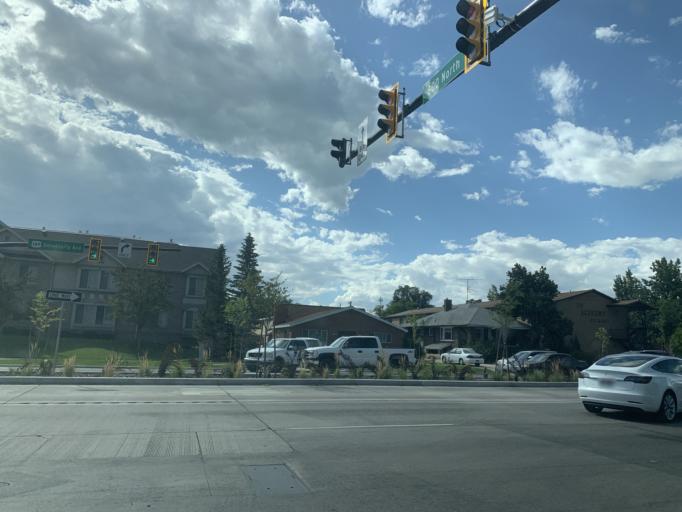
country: US
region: Utah
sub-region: Utah County
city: Provo
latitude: 40.2418
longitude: -111.6584
